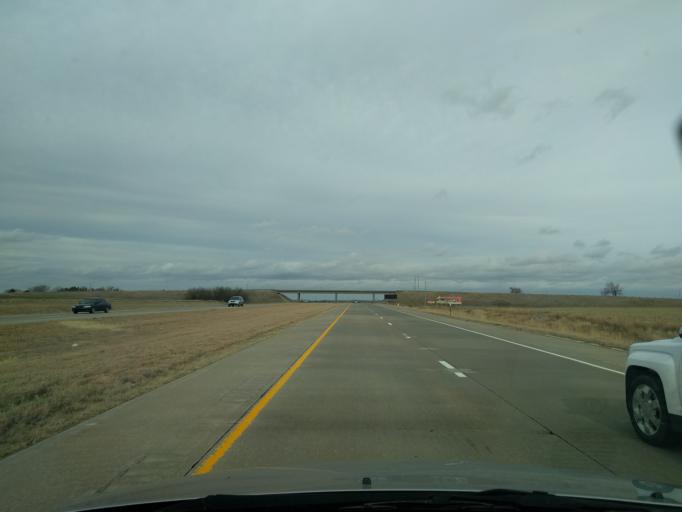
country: US
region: Kansas
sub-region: Saline County
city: Salina
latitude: 38.7080
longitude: -97.6218
